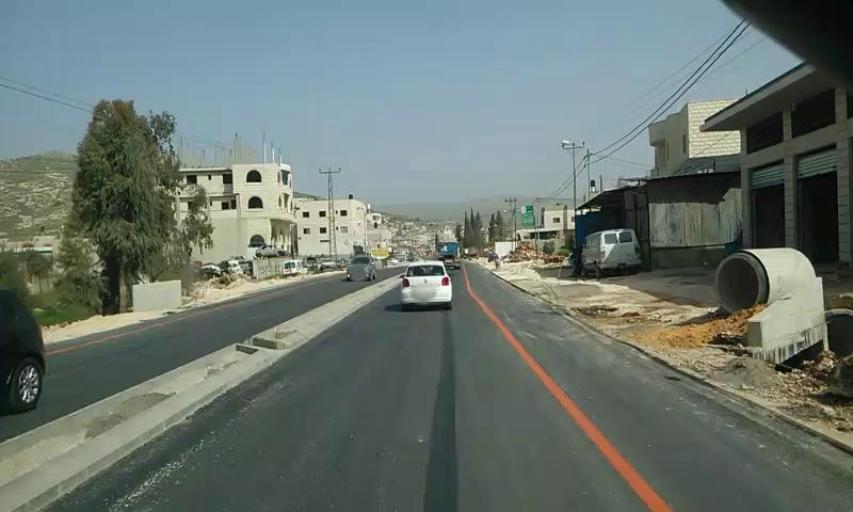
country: PS
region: West Bank
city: Huwwarah
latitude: 32.1418
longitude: 35.2581
